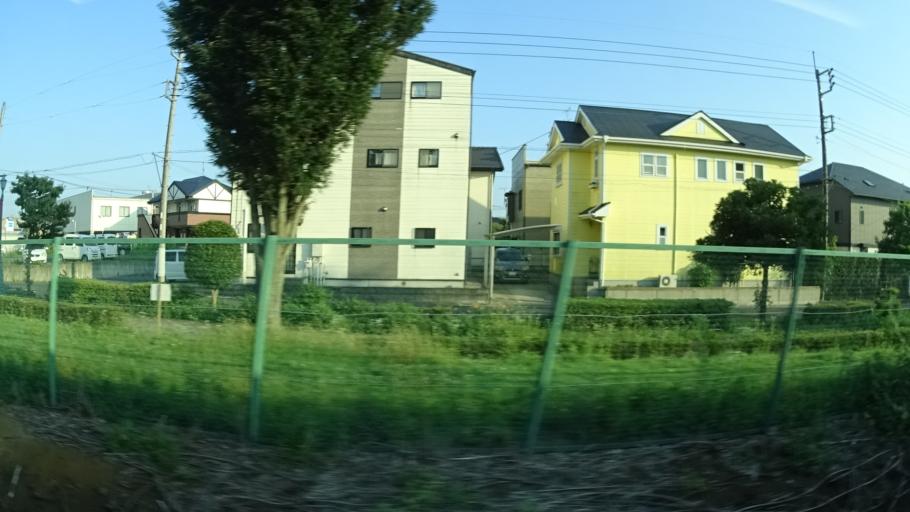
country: JP
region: Ibaraki
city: Mito-shi
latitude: 36.3812
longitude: 140.4102
